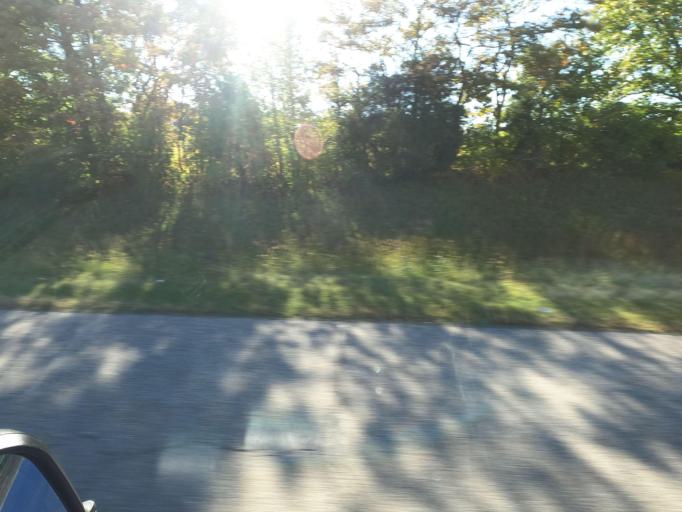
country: US
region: Tennessee
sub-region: Crockett County
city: Alamo
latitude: 35.7587
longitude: -89.1146
